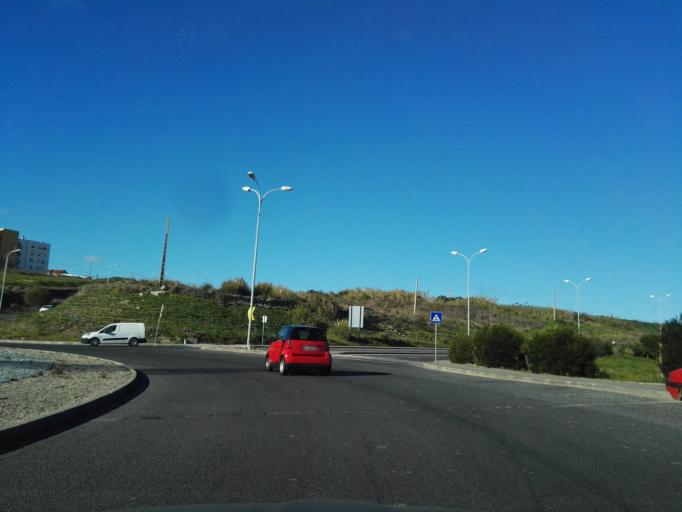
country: PT
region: Lisbon
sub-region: Odivelas
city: Famoes
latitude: 38.7808
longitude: -9.2203
